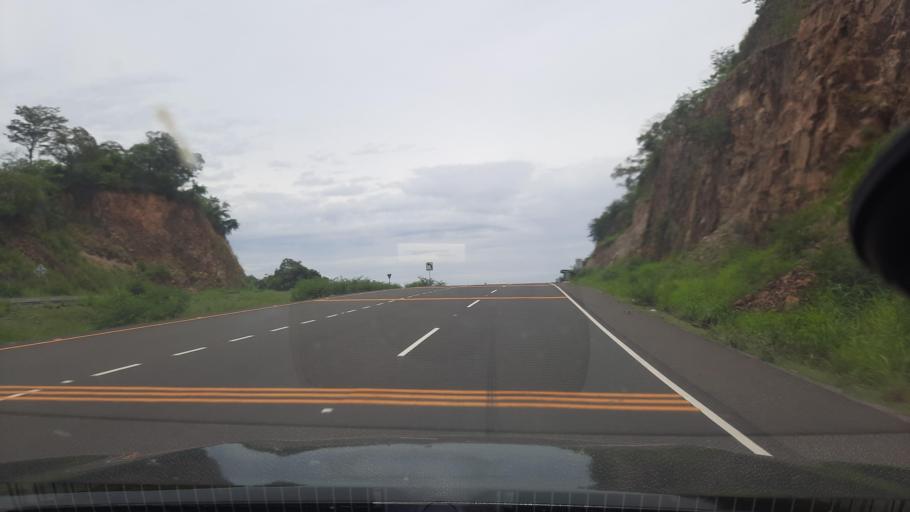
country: HN
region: Valle
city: Aramecina
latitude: 13.7484
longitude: -87.7161
